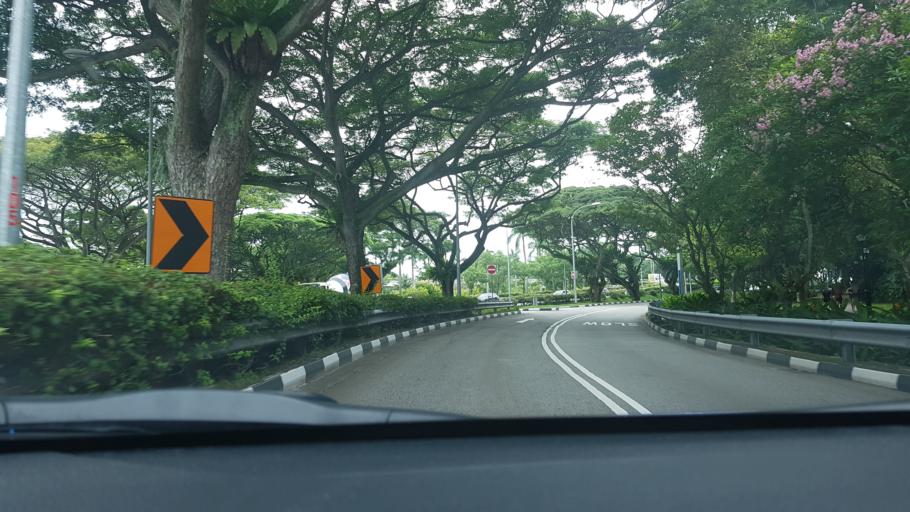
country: SG
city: Singapore
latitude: 1.3005
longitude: 103.9081
